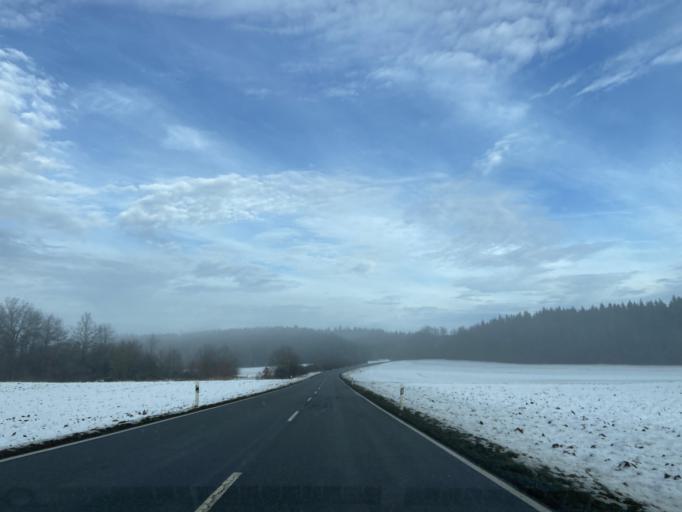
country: DE
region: Baden-Wuerttemberg
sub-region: Tuebingen Region
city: Hettingen
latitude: 48.2183
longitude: 9.2852
